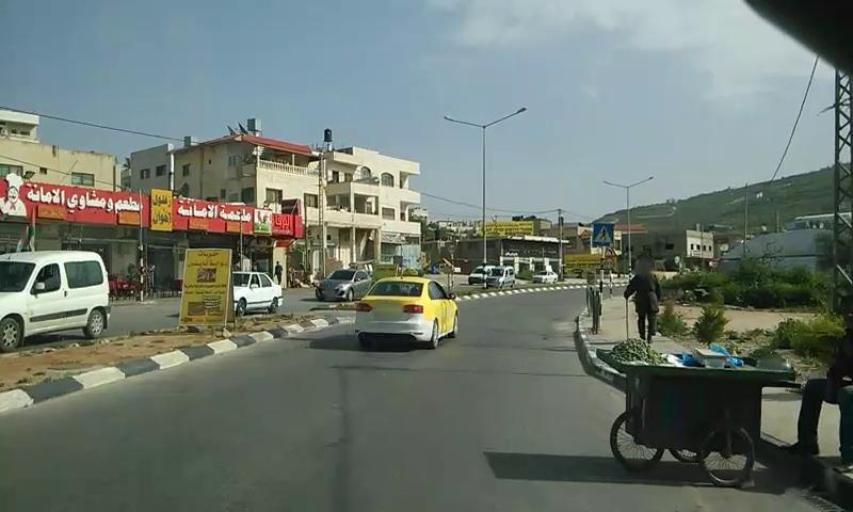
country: PS
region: West Bank
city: Dayr Sharaf
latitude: 32.2542
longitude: 35.1858
